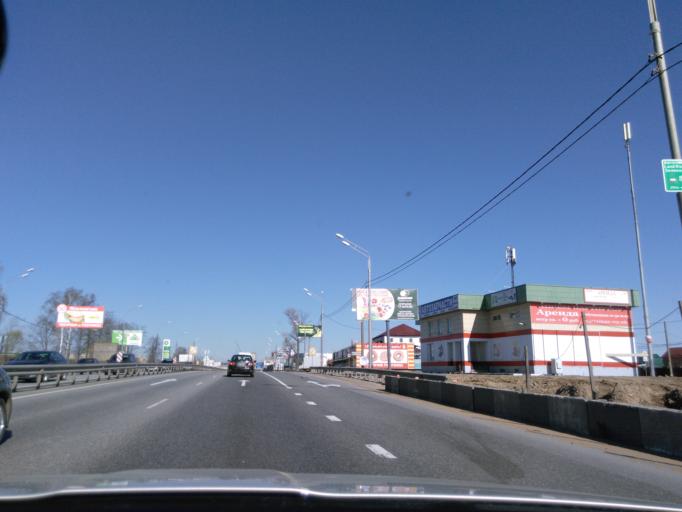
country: RU
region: Moskovskaya
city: Rzhavki
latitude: 55.9949
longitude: 37.2573
